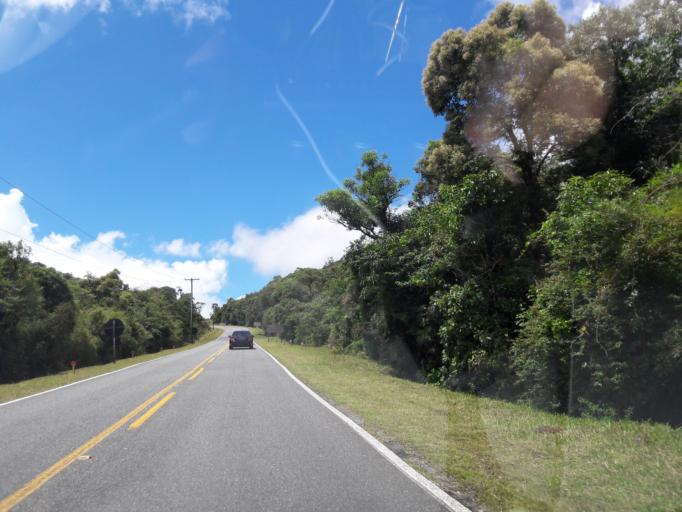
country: BR
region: Parana
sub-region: Campina Grande Do Sul
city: Campina Grande do Sul
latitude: -25.3329
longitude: -48.9090
